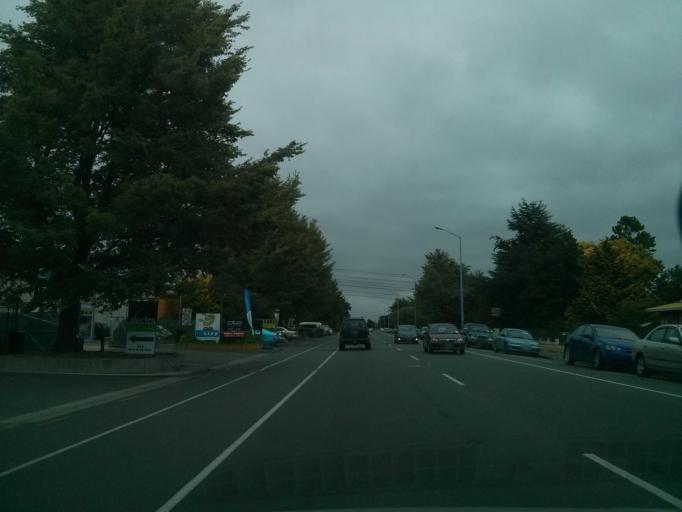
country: NZ
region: Canterbury
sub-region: Selwyn District
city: Prebbleton
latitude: -43.5366
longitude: 172.5588
